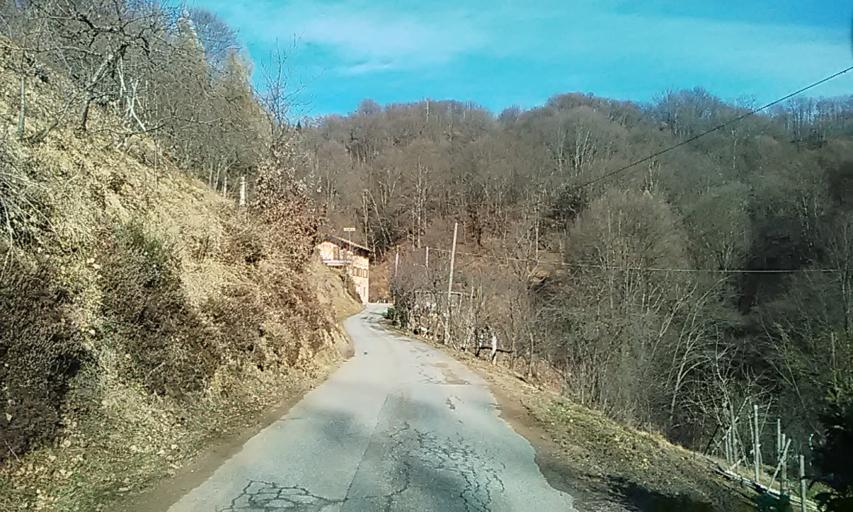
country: IT
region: Piedmont
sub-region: Provincia di Vercelli
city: Cellio
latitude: 45.7372
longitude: 8.3119
